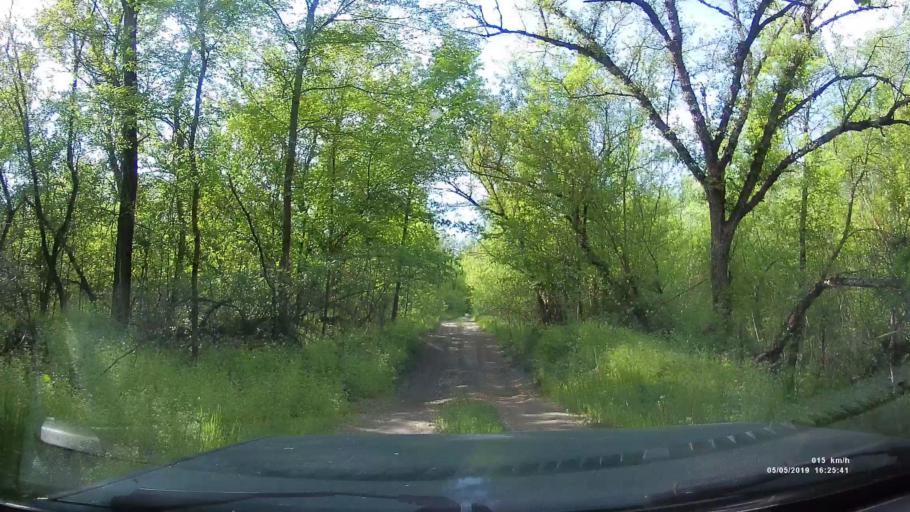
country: RU
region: Rostov
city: Konstantinovsk
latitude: 47.7620
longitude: 41.0229
